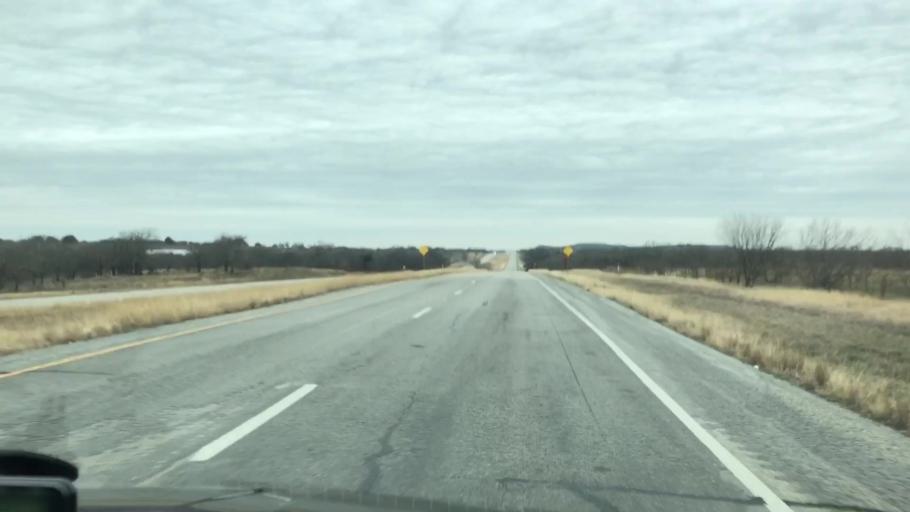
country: US
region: Texas
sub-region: Jack County
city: Jacksboro
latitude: 33.2388
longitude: -98.2136
